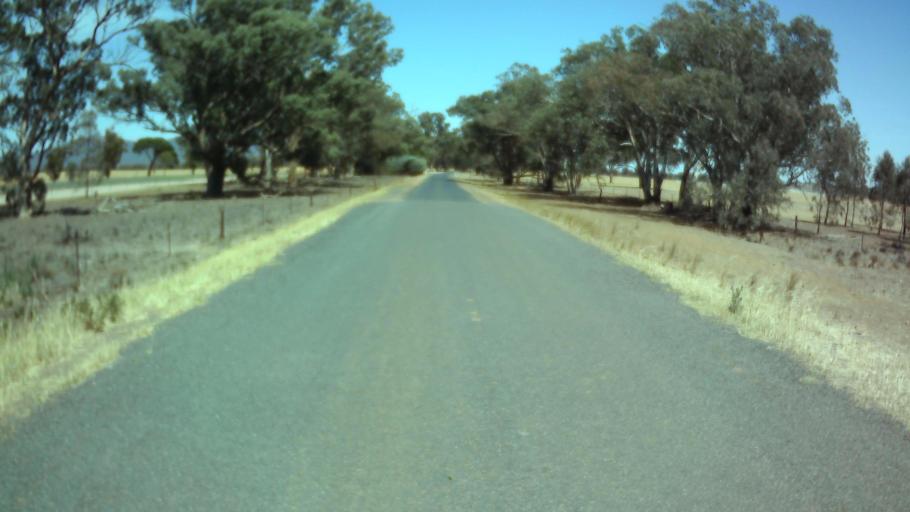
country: AU
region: New South Wales
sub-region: Weddin
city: Grenfell
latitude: -33.8685
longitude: 148.0748
